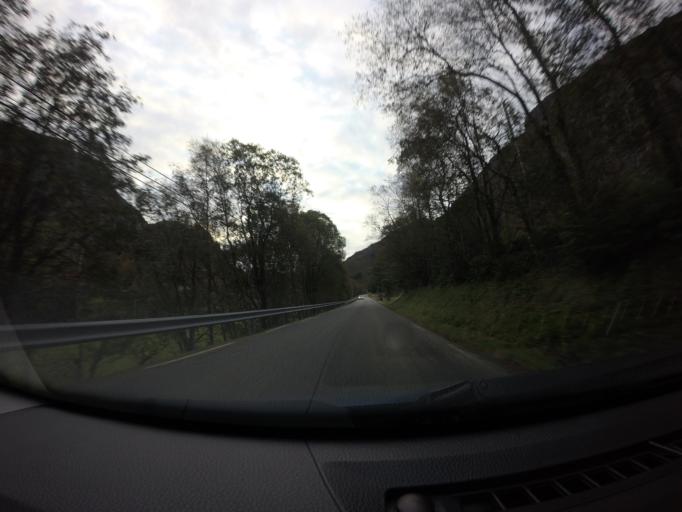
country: NO
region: Rogaland
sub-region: Forsand
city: Forsand
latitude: 58.8120
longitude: 6.2307
